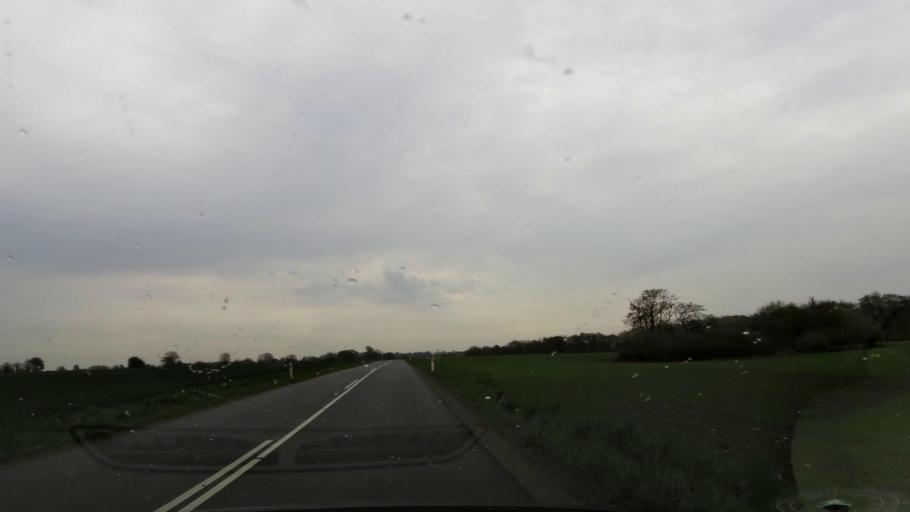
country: DK
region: South Denmark
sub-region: Svendborg Kommune
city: Svendborg
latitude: 55.1641
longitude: 10.6448
